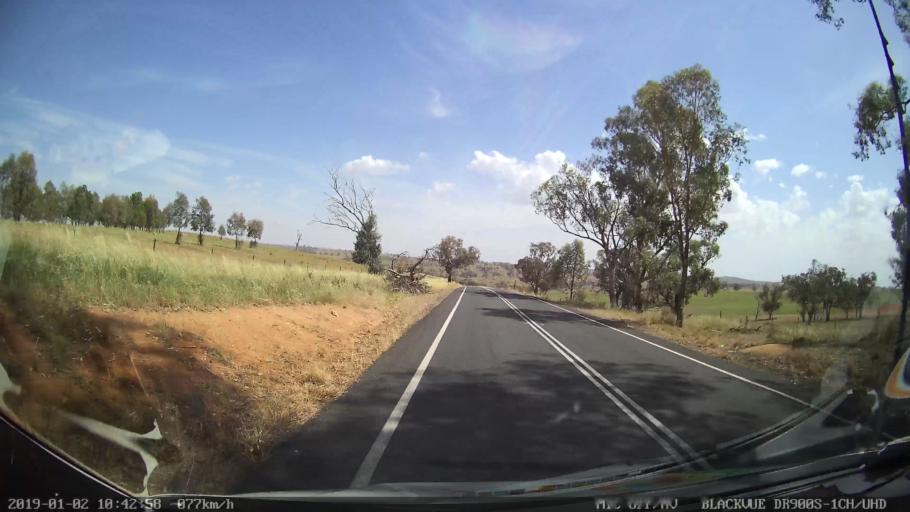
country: AU
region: New South Wales
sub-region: Cootamundra
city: Cootamundra
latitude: -34.7781
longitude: 148.3062
